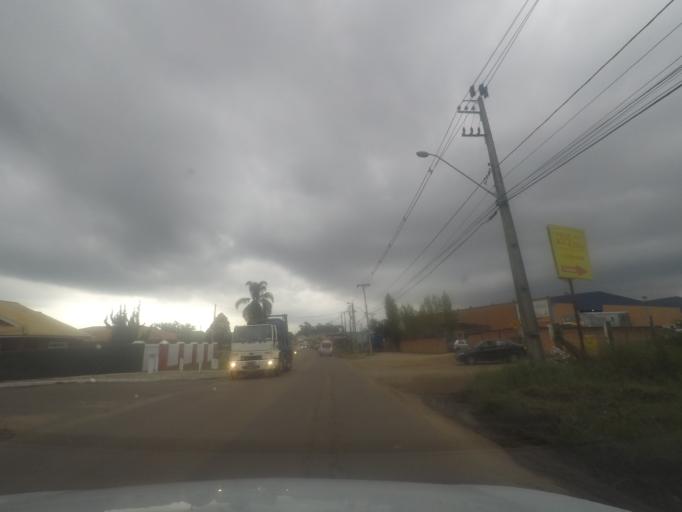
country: BR
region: Parana
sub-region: Sao Jose Dos Pinhais
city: Sao Jose dos Pinhais
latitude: -25.5604
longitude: -49.2688
